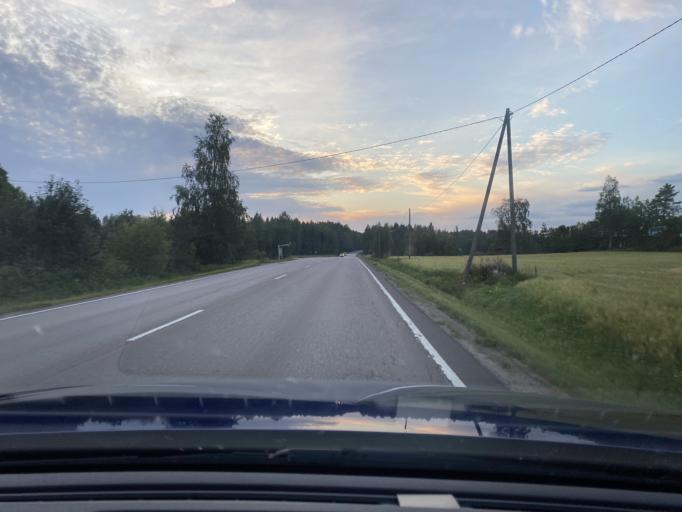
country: FI
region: Satakunta
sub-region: Pohjois-Satakunta
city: Honkajoki
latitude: 61.9040
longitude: 22.2733
